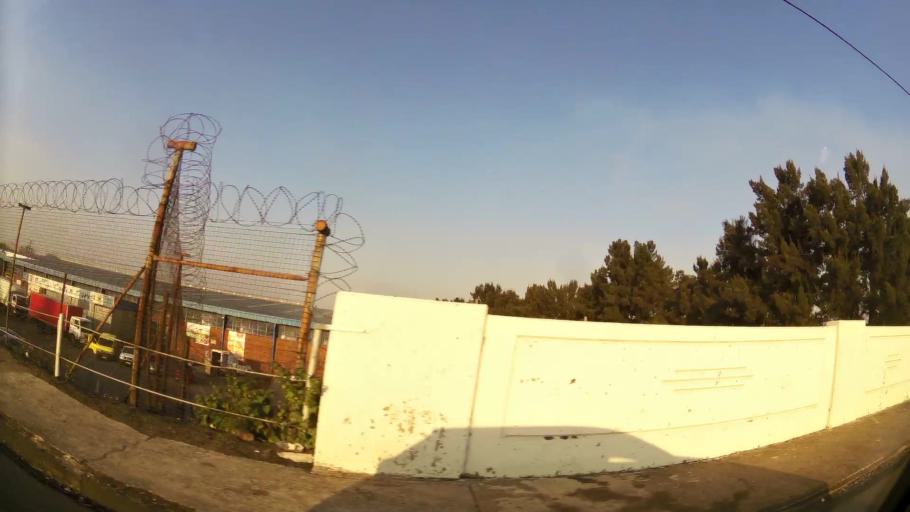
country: ZA
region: Gauteng
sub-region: Ekurhuleni Metropolitan Municipality
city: Springs
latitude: -26.2648
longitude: 28.4175
